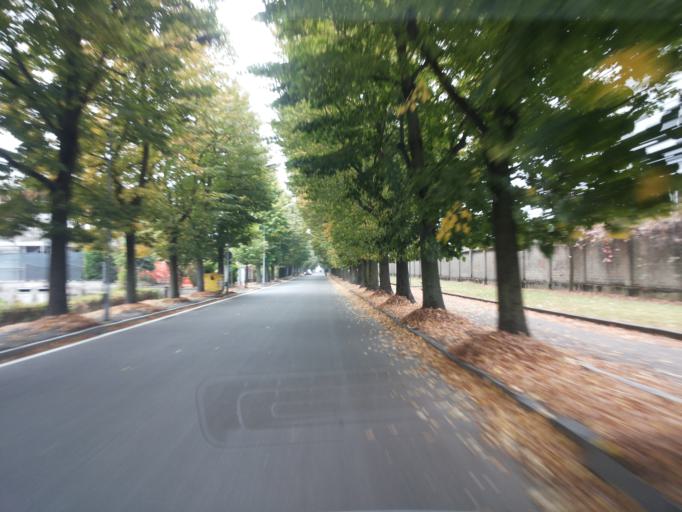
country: IT
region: Piedmont
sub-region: Provincia di Vercelli
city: Vercelli
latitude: 45.3327
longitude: 8.4350
